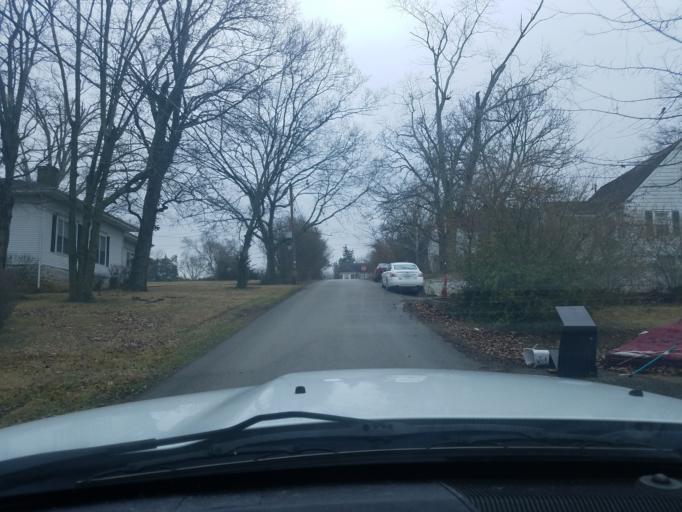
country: US
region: Kentucky
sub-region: Logan County
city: Russellville
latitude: 36.8430
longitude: -86.8792
